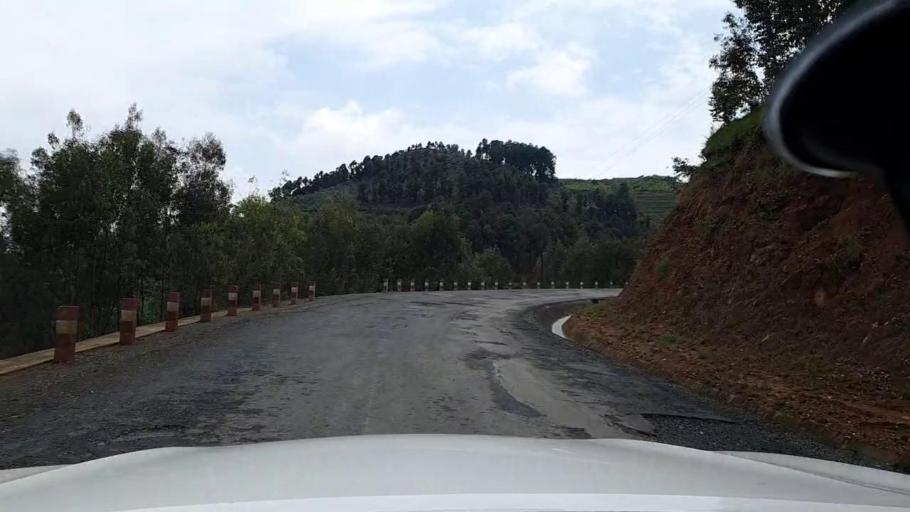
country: RW
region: Southern Province
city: Gitarama
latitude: -2.0617
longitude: 29.5632
